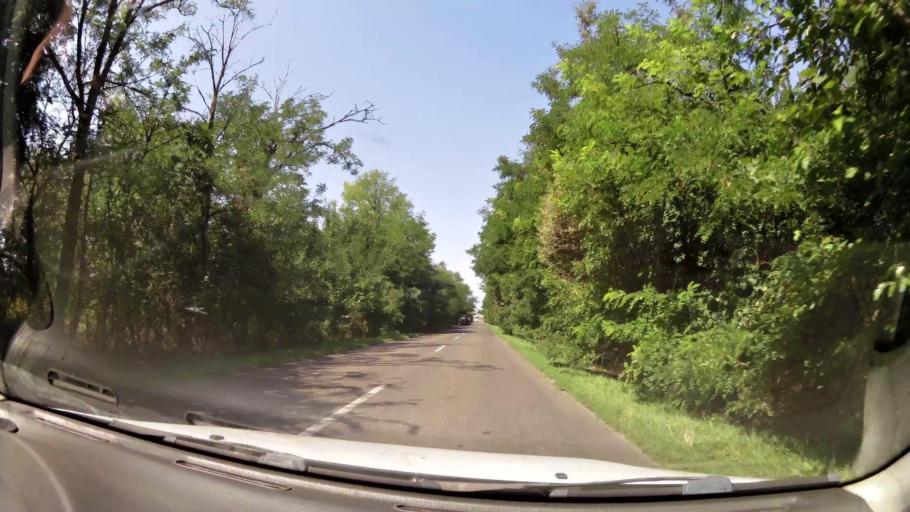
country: HU
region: Pest
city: Tapiosag
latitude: 47.3939
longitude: 19.6384
